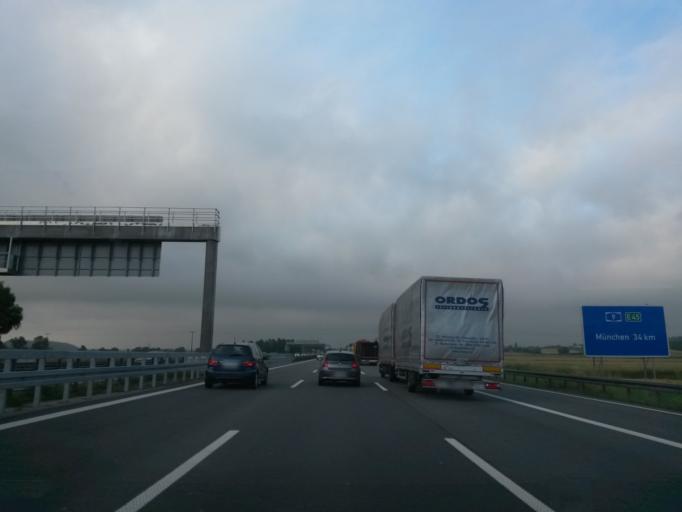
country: DE
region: Bavaria
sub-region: Upper Bavaria
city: Allershausen
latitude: 48.4207
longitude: 11.5894
